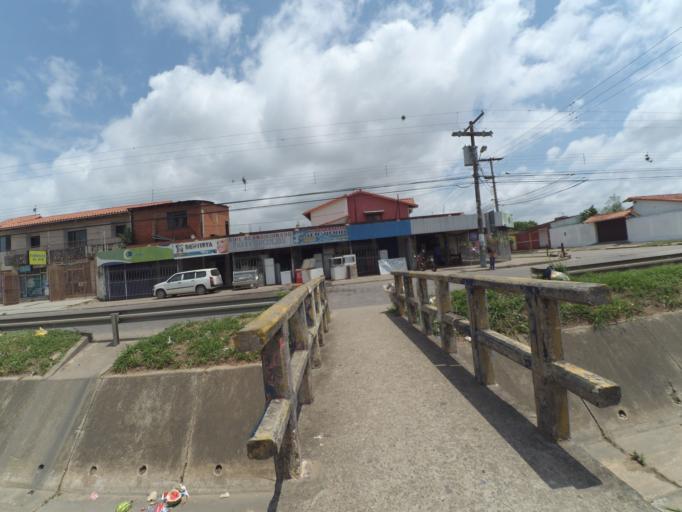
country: BO
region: Santa Cruz
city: Santa Cruz de la Sierra
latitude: -17.7967
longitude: -63.2126
